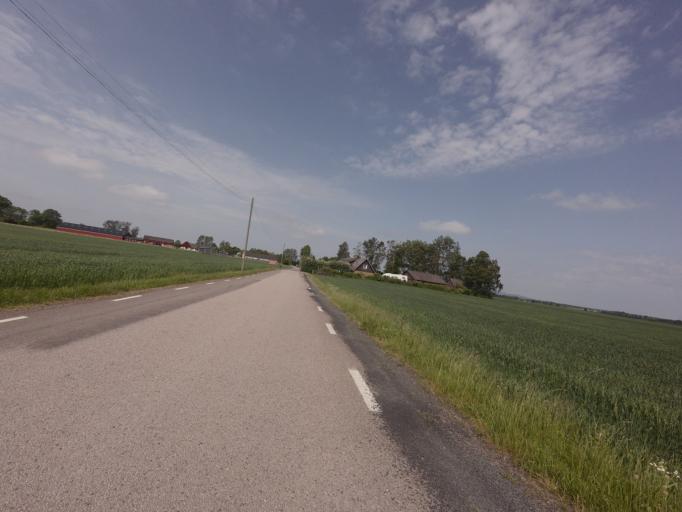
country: SE
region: Skane
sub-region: Hoganas Kommun
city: Hoganas
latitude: 56.1860
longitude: 12.6563
